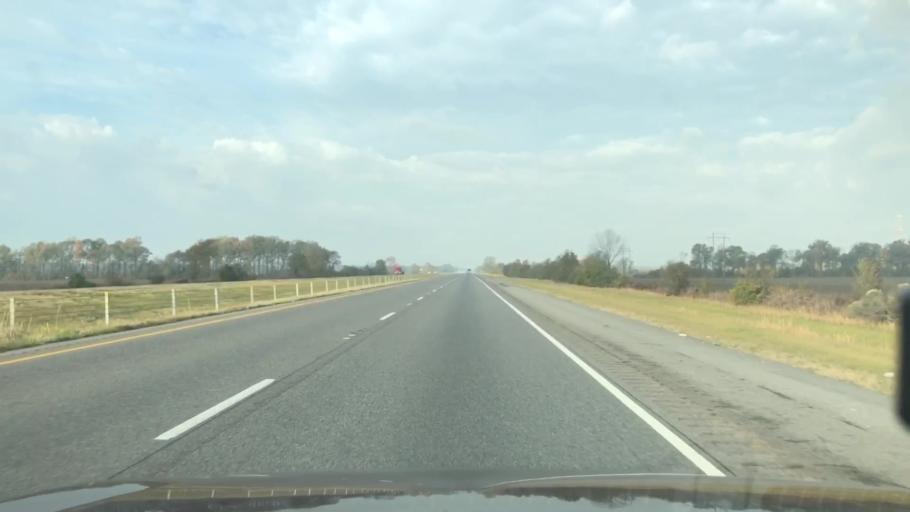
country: US
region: Louisiana
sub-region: Madison Parish
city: Tallulah
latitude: 32.4216
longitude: -91.3287
